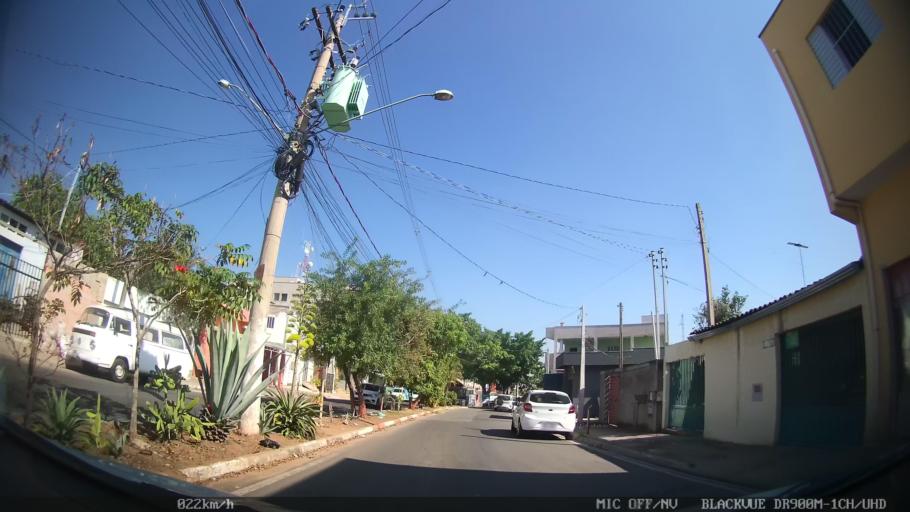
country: BR
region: Sao Paulo
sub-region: Campinas
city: Campinas
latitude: -22.9383
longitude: -47.0784
